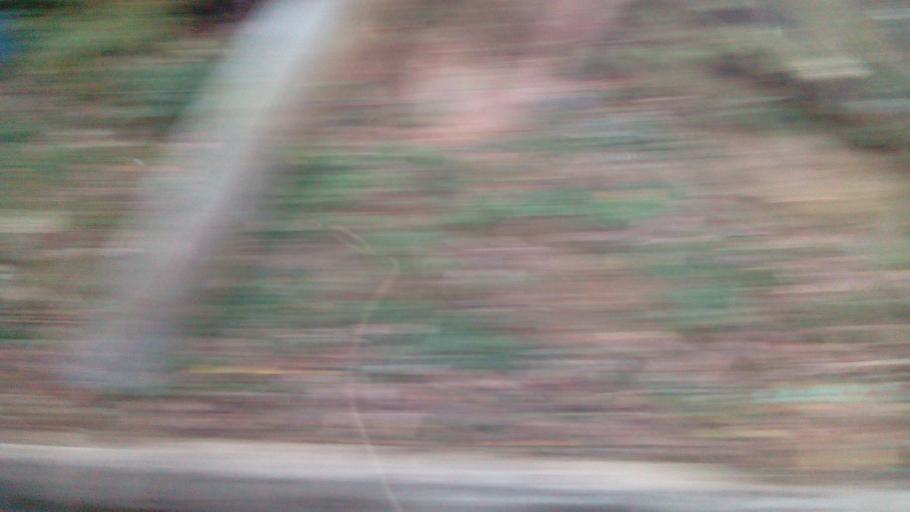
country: TW
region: Taiwan
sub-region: Hualien
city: Hualian
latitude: 24.3382
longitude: 121.3127
